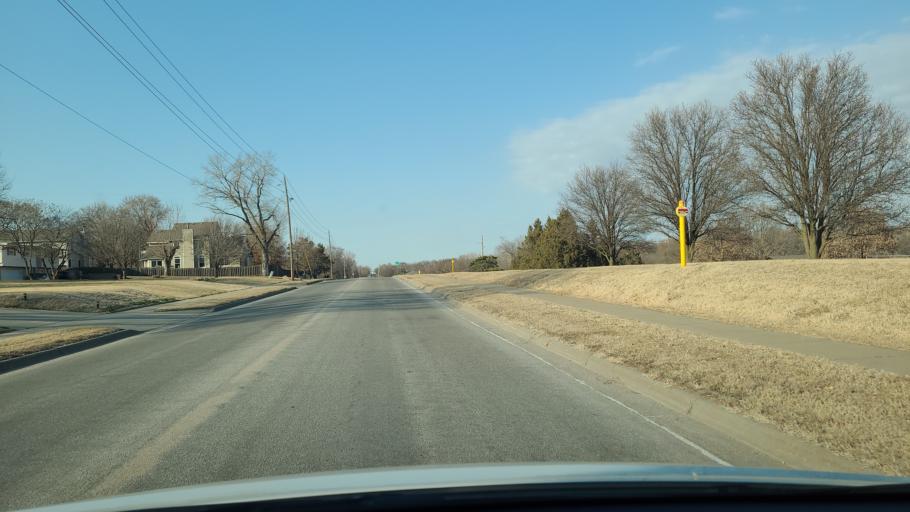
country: US
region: Kansas
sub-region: Douglas County
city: Lawrence
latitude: 38.9608
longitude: -95.2883
